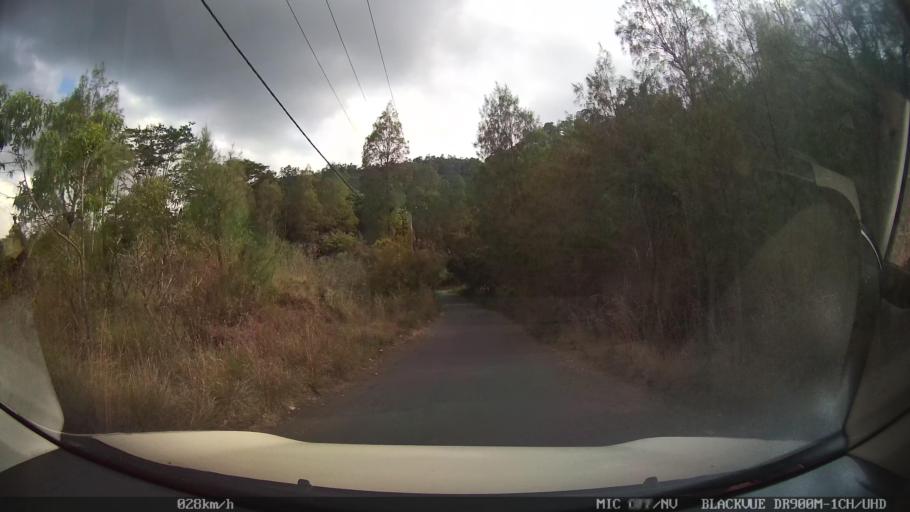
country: ID
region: Bali
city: Banjar Kedisan
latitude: -8.2454
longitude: 115.3486
